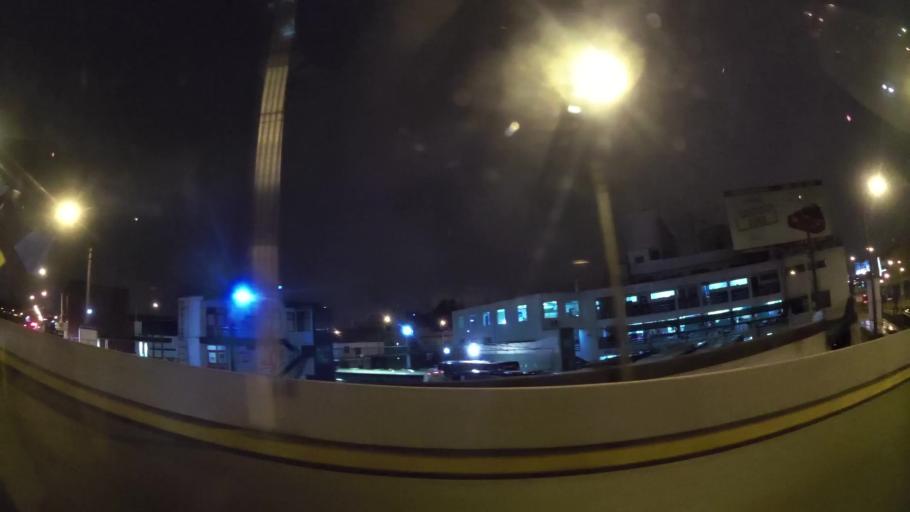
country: PE
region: Lima
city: Lima
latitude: -12.0767
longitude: -77.0281
